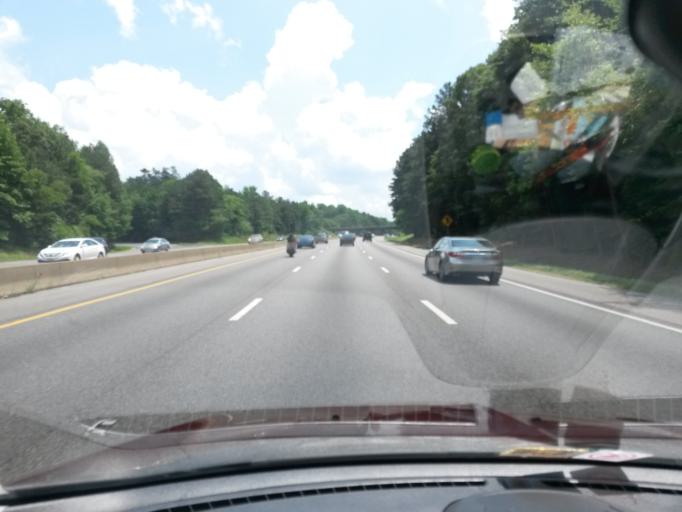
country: US
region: Virginia
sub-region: Chesterfield County
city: Chester
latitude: 37.3774
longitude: -77.4084
